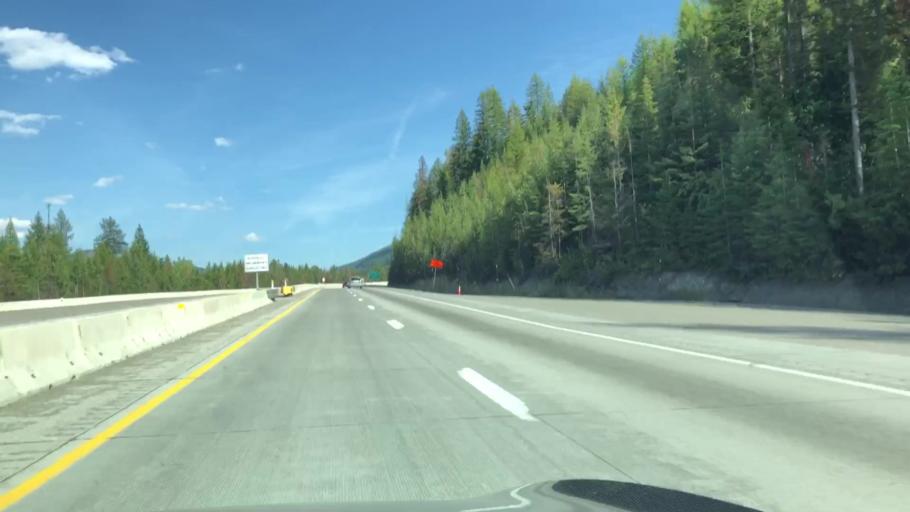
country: US
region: Idaho
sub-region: Shoshone County
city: Wallace
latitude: 47.4650
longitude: -115.7541
